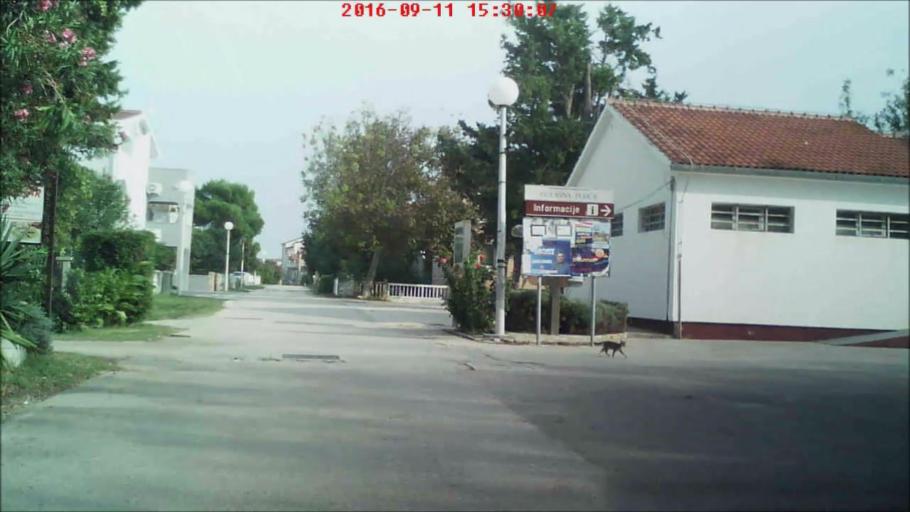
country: HR
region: Zadarska
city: Nin
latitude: 44.2587
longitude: 15.1607
